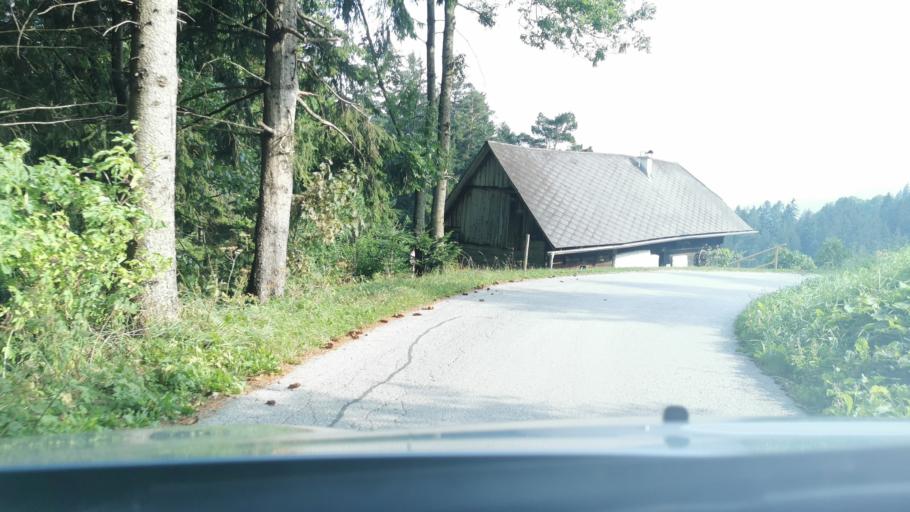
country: AT
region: Styria
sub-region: Politischer Bezirk Weiz
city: Fischbach
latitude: 47.3980
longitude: 15.6444
